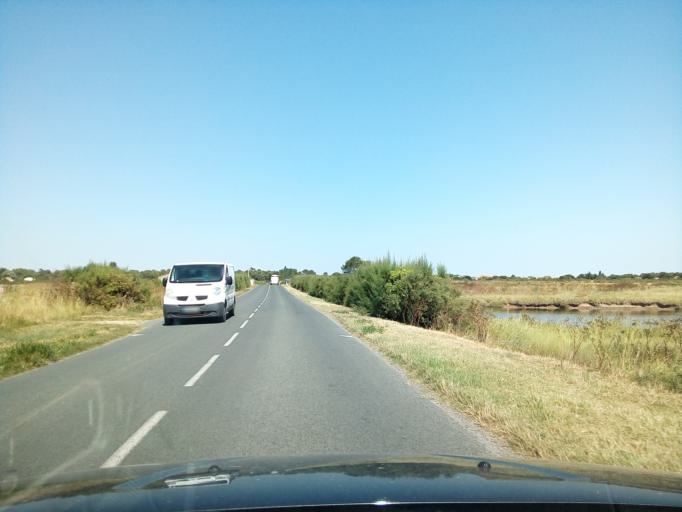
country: FR
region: Poitou-Charentes
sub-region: Departement de la Charente-Maritime
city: Boyard-Ville
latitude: 45.9661
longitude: -1.2559
